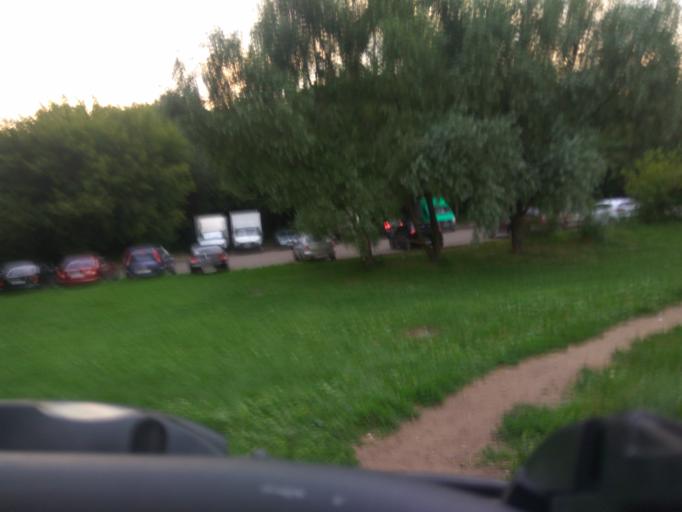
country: RU
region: Moscow
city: Brateyevo
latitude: 55.6412
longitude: 37.7748
